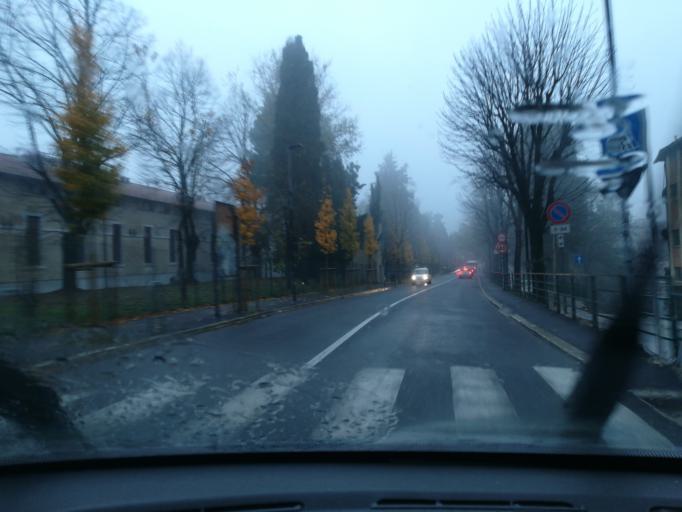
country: IT
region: The Marches
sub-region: Provincia di Macerata
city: Macerata
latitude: 43.2984
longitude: 13.4336
